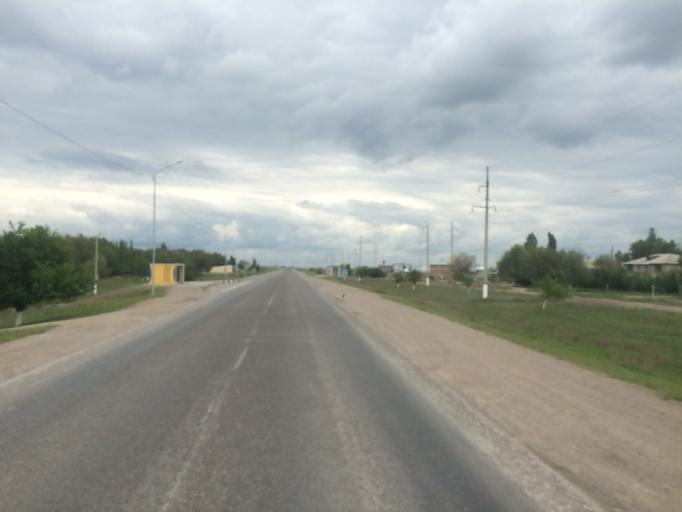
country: KG
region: Chuy
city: Sokuluk
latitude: 43.2494
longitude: 74.2913
